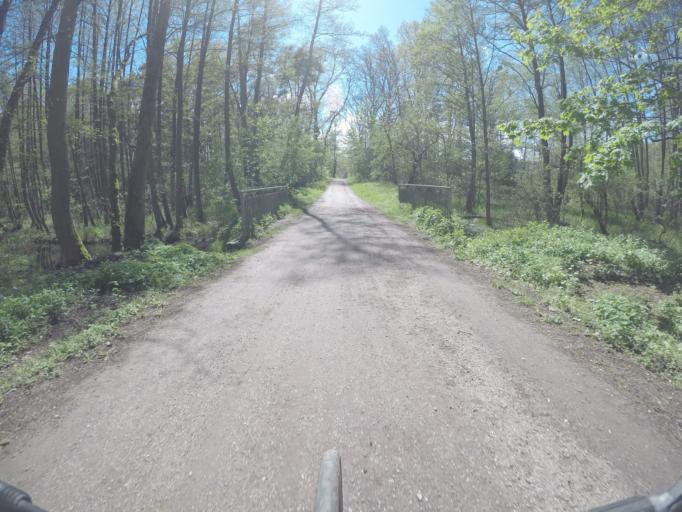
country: DE
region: Brandenburg
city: Biesenthal
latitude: 52.7533
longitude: 13.6232
